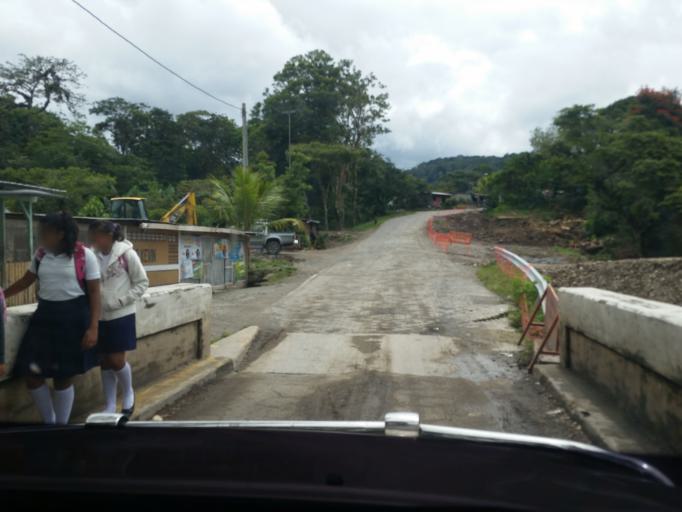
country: NI
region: Jinotega
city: Jinotega
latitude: 13.1798
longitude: -85.9111
